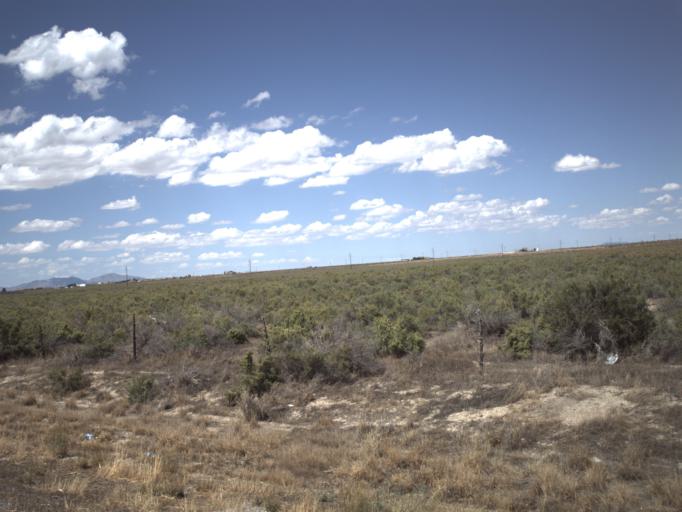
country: US
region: Utah
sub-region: Millard County
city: Delta
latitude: 39.3531
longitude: -112.5196
